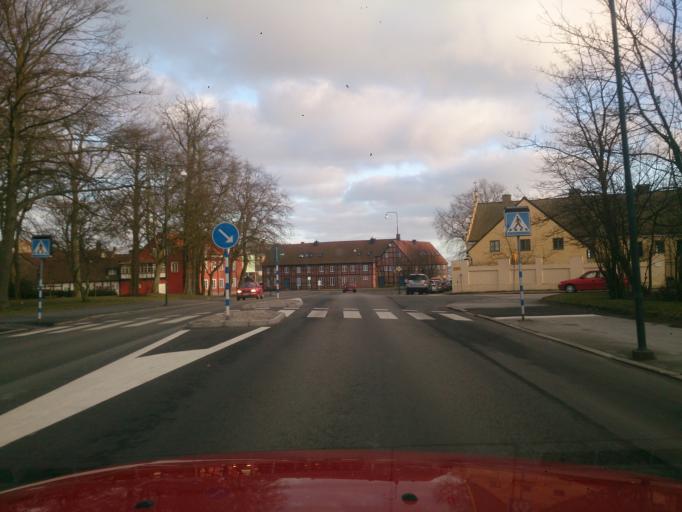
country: SE
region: Skane
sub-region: Ystads Kommun
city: Ystad
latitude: 55.4277
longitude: 13.8103
